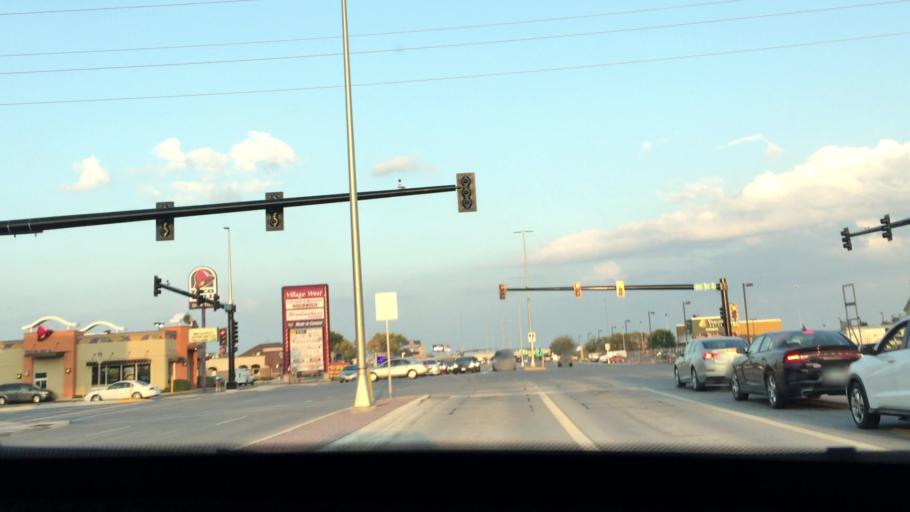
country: US
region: North Dakota
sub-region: Cass County
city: West Fargo
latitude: 46.8618
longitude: -96.8516
